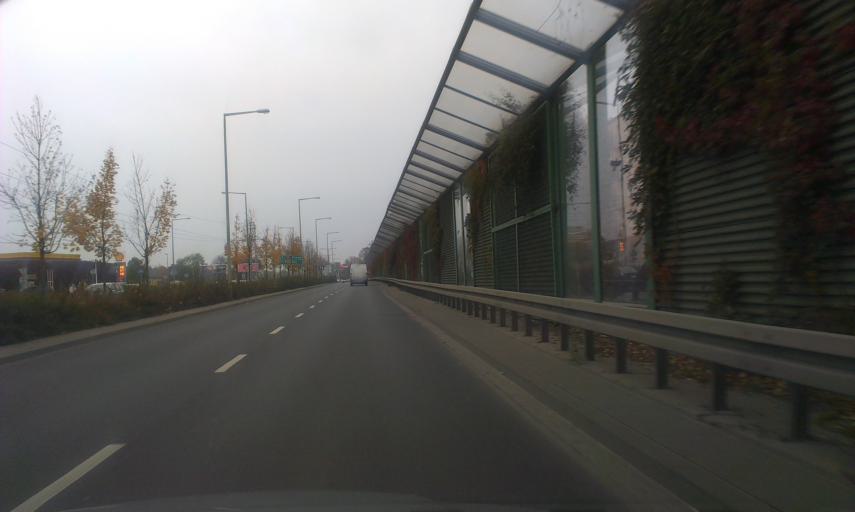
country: PL
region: Greater Poland Voivodeship
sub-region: Poznan
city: Poznan
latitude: 52.4096
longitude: 16.8686
